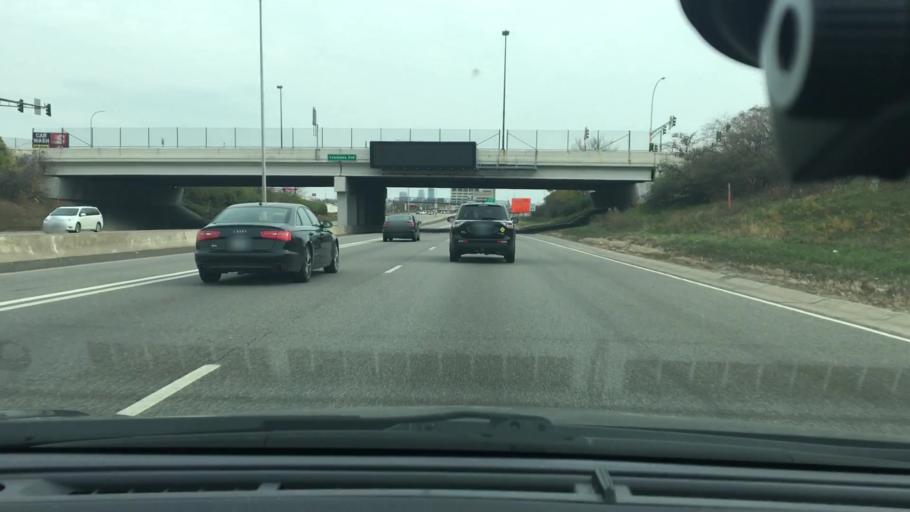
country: US
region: Minnesota
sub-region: Hennepin County
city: Saint Louis Park
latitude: 44.9712
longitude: -93.3718
